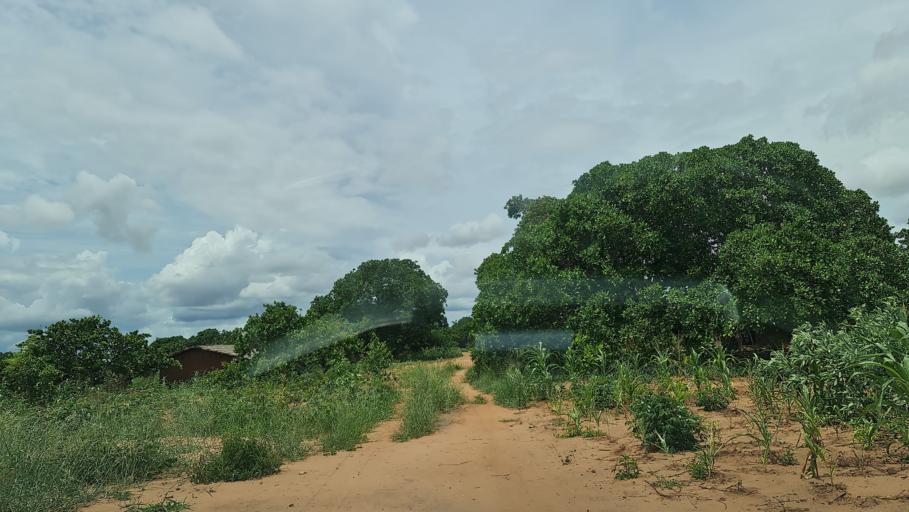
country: MZ
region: Nampula
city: Nacala
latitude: -14.7911
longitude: 39.9664
